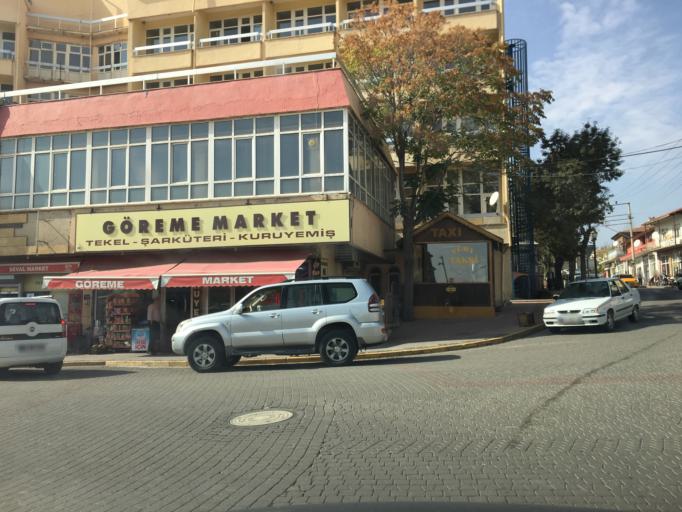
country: TR
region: Nevsehir
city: Avanos
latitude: 38.7172
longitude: 34.8436
